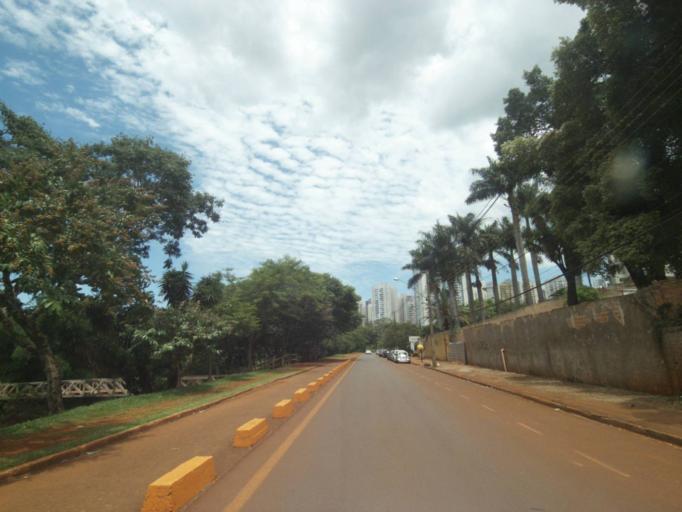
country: BR
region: Parana
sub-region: Londrina
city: Londrina
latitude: -23.3222
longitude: -51.1823
